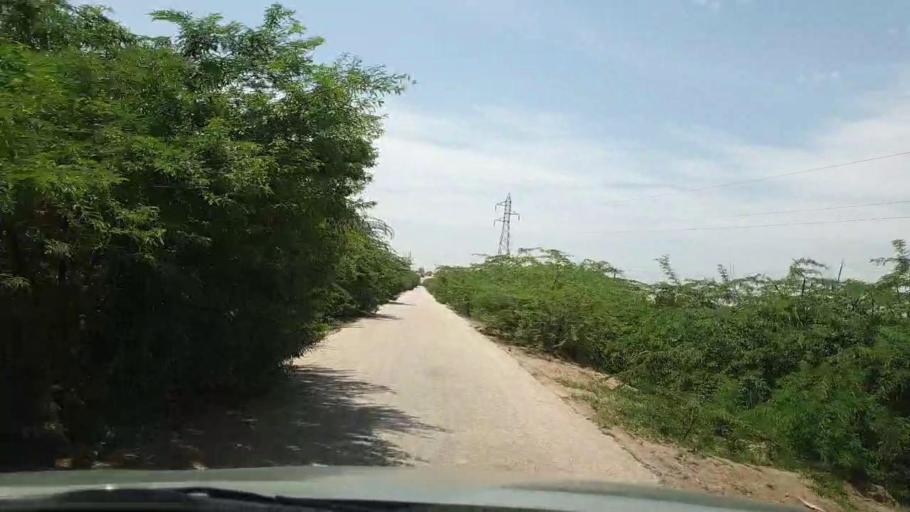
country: PK
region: Sindh
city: Bozdar
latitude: 27.0836
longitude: 68.9662
